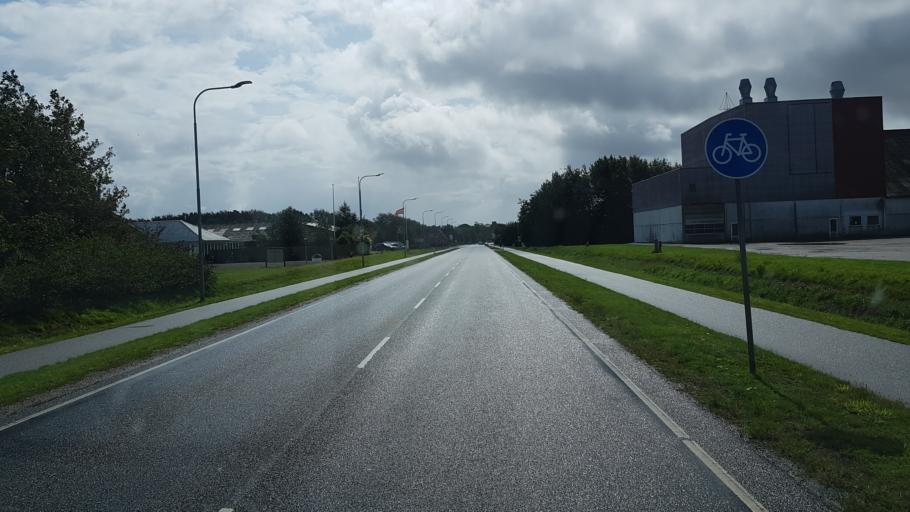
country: DK
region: South Denmark
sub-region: Vejen Kommune
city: Holsted
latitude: 55.4926
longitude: 8.9148
